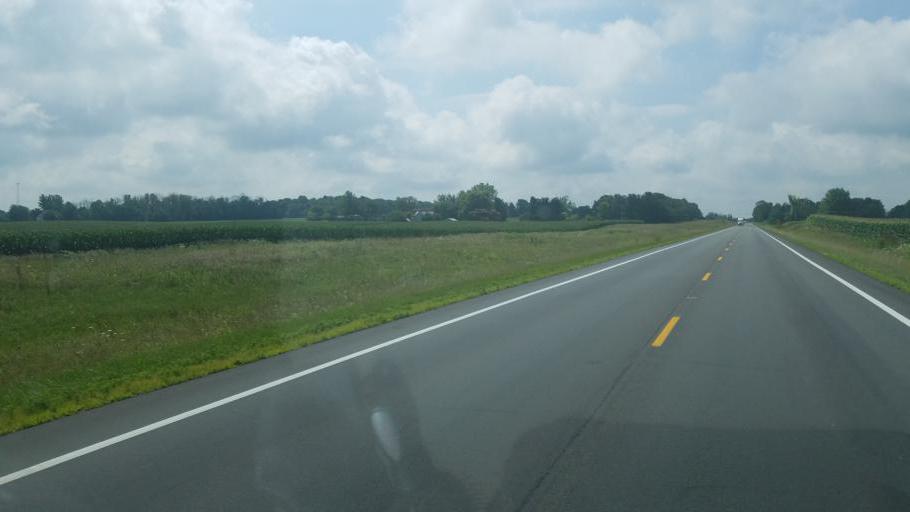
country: US
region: Ohio
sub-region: Fairfield County
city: Baltimore
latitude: 39.7859
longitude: -82.5734
